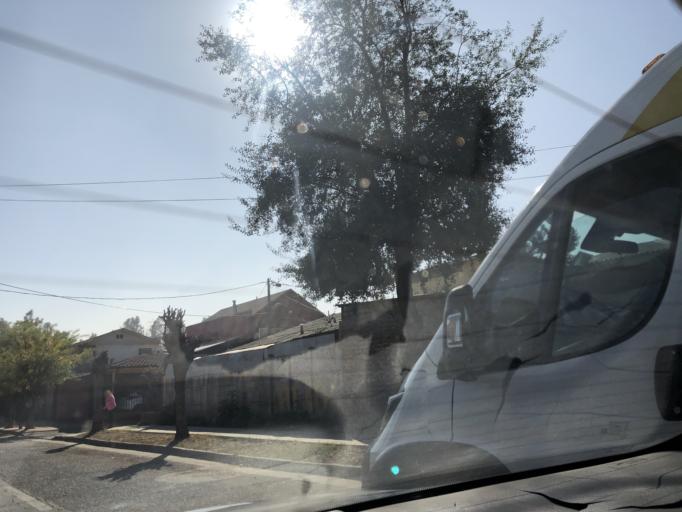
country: CL
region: Santiago Metropolitan
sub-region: Provincia de Cordillera
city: Puente Alto
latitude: -33.5788
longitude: -70.5864
